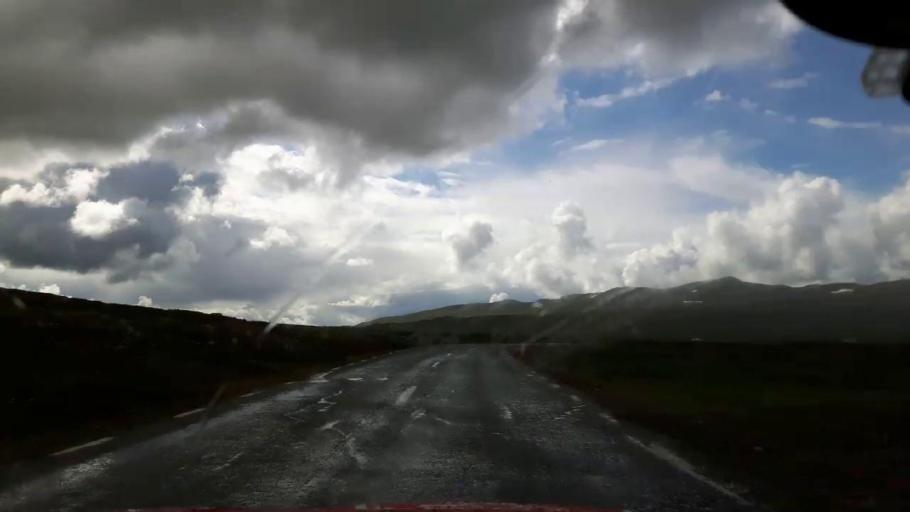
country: NO
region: Nordland
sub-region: Hattfjelldal
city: Hattfjelldal
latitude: 65.0874
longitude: 14.4586
